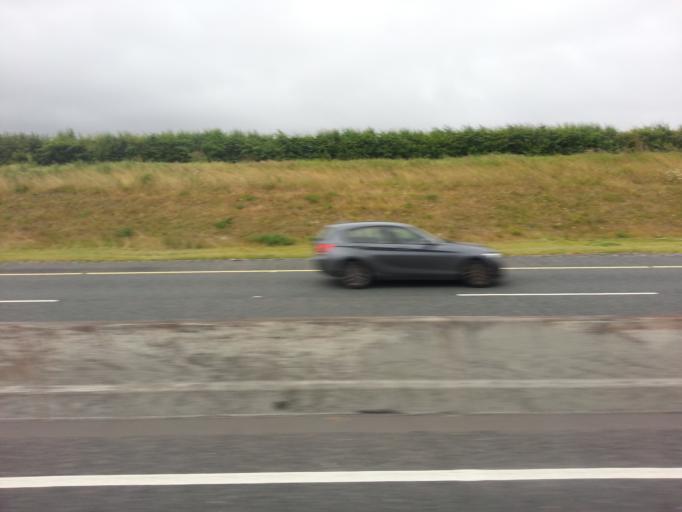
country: IE
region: Leinster
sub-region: County Carlow
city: Carlow
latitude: 52.8227
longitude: -6.8486
